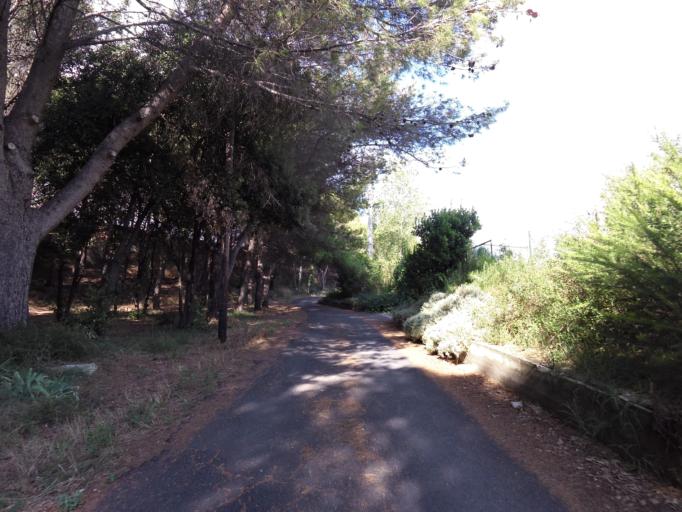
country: FR
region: Languedoc-Roussillon
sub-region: Departement du Gard
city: Gallargues-le-Montueux
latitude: 43.7241
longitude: 4.1679
